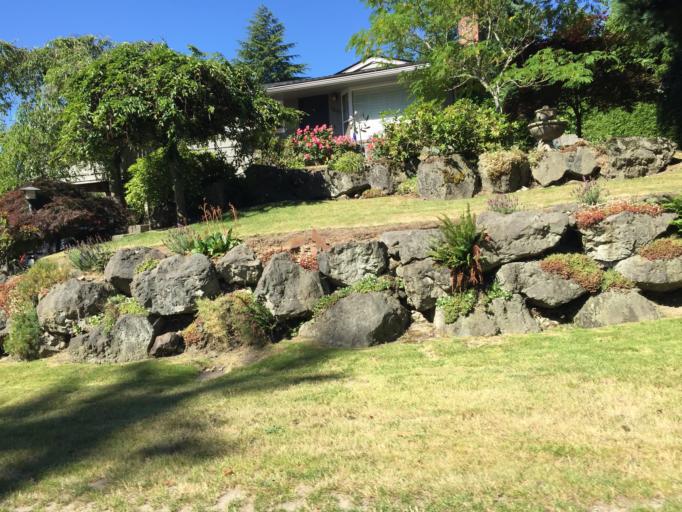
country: US
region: Washington
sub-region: King County
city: Bellevue
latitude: 47.6242
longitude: -122.2050
